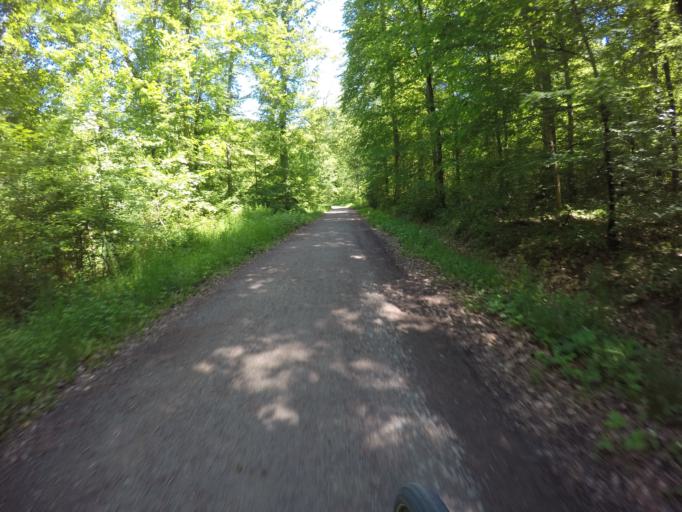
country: DE
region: Baden-Wuerttemberg
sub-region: Regierungsbezirk Stuttgart
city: Gerlingen
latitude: 48.7413
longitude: 9.0746
